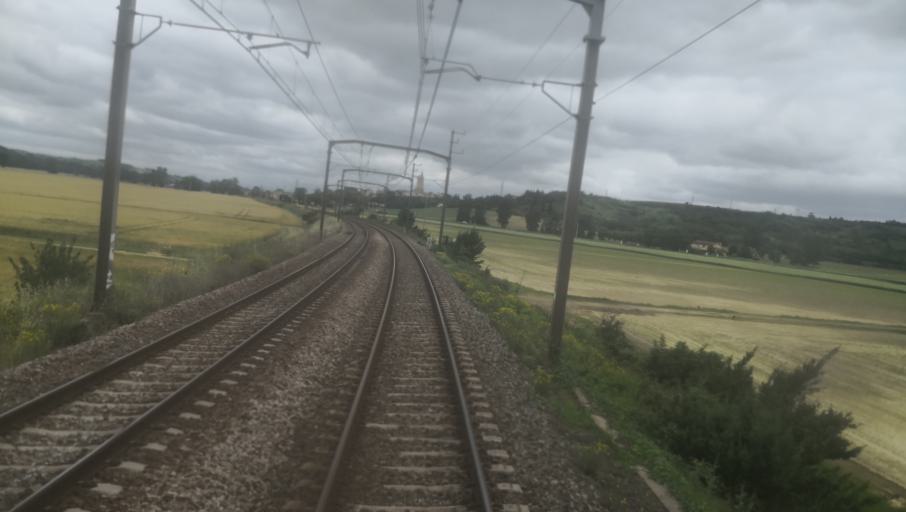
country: FR
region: Midi-Pyrenees
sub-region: Departement de la Haute-Garonne
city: Avignonet-Lauragais
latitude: 43.3599
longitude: 1.8022
